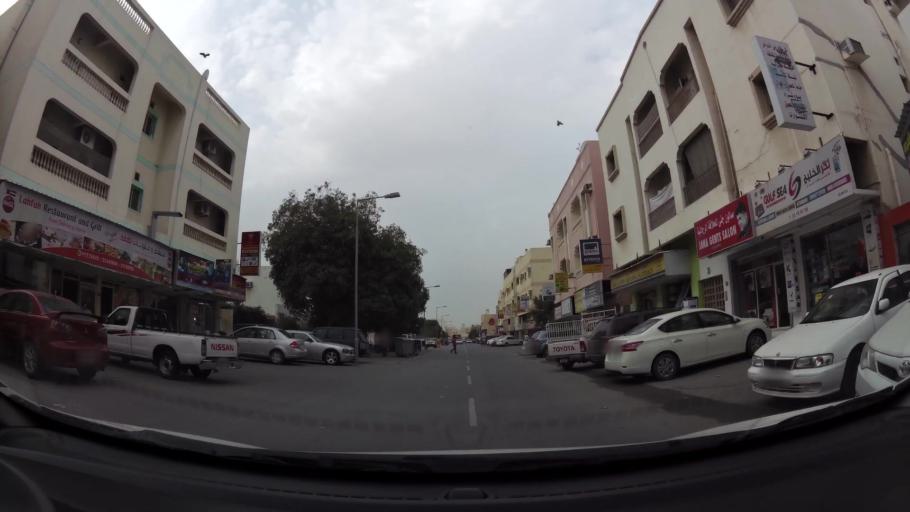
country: BH
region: Northern
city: Ar Rifa'
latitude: 26.1261
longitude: 50.5789
